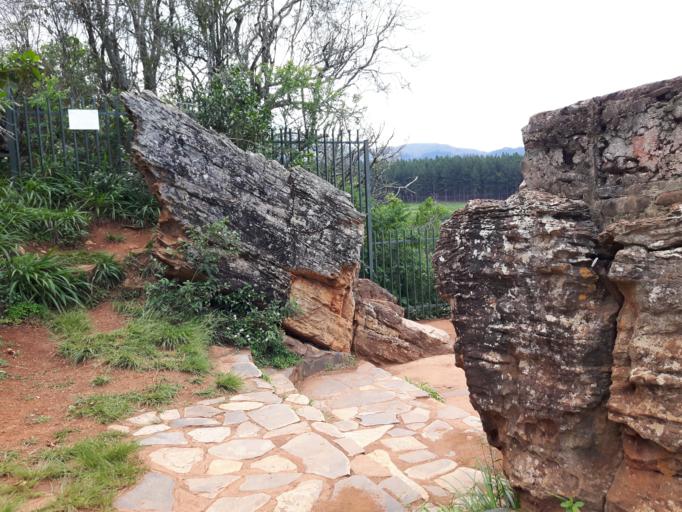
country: ZA
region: Mpumalanga
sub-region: Ehlanzeni District
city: Graksop
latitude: -25.0008
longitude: 30.8173
